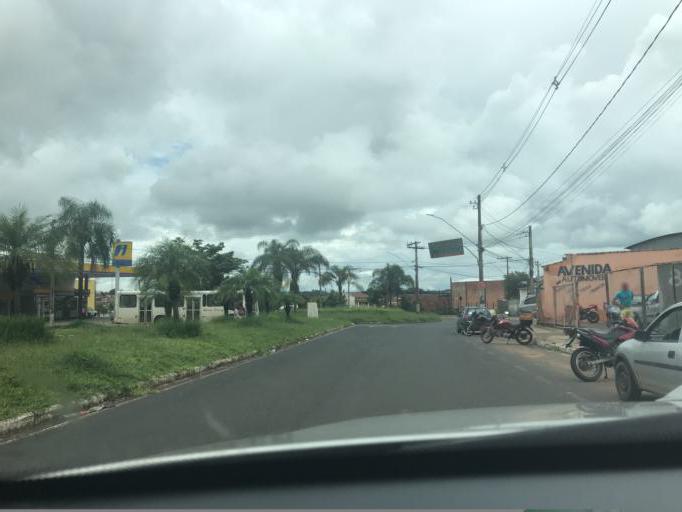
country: BR
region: Minas Gerais
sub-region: Araxa
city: Araxa
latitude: -19.5807
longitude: -46.9362
